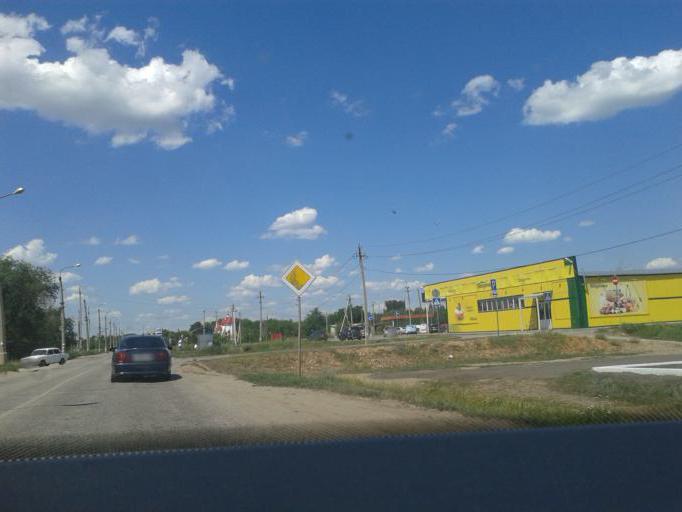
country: RU
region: Volgograd
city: Frolovo
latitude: 49.7510
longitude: 43.6538
